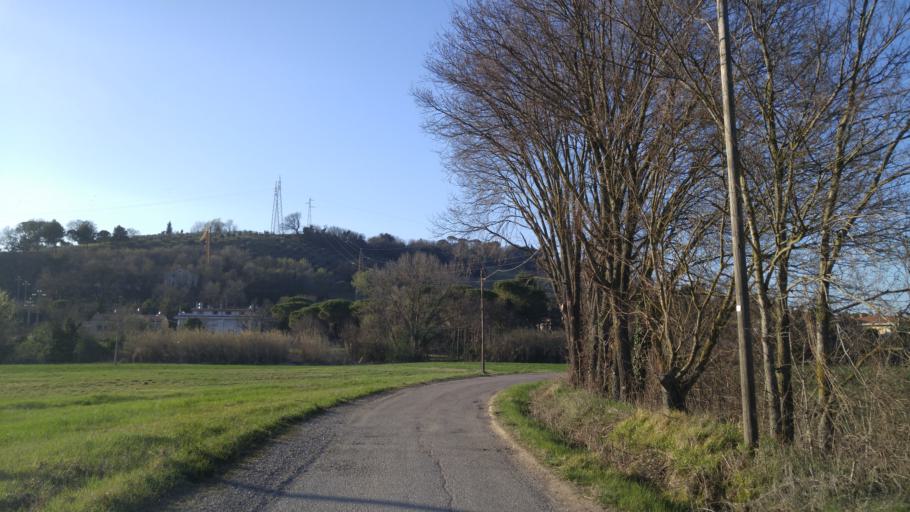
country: IT
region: The Marches
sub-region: Provincia di Pesaro e Urbino
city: Pesaro
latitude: 43.8795
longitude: 12.9020
